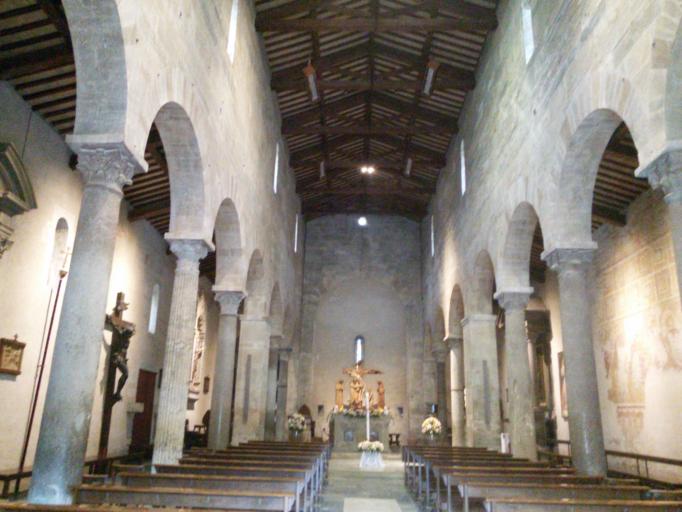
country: IT
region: Tuscany
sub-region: Province of Pisa
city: Vicopisano
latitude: 43.7003
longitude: 10.5834
